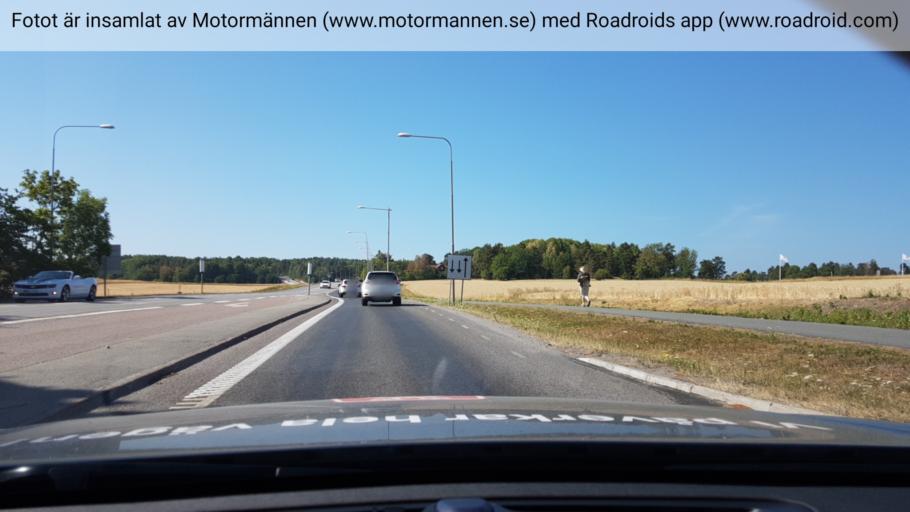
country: SE
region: Stockholm
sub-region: Ekero Kommun
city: Ekeroe
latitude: 59.3199
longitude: 17.8670
